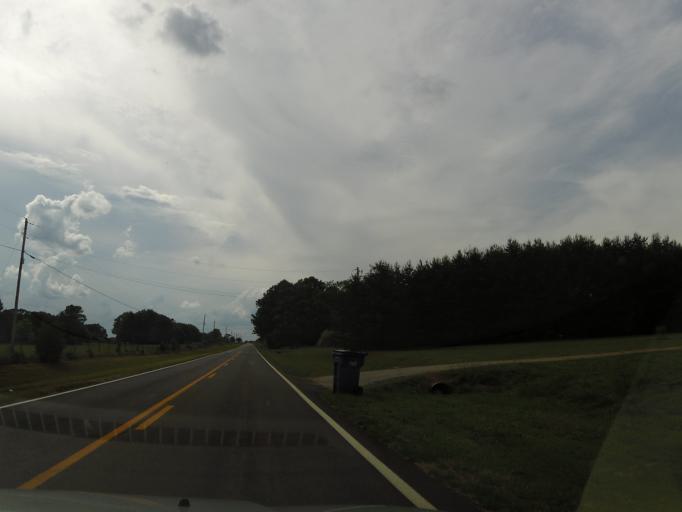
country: US
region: Georgia
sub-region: McDuffie County
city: Thomson
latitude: 33.5249
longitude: -82.4683
